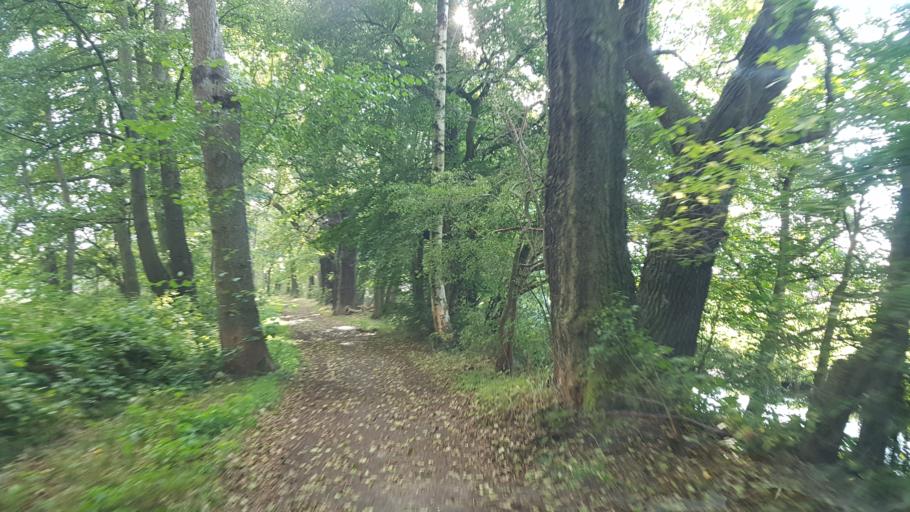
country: DE
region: Saxony
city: Dahlen
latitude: 51.3877
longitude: 12.9983
